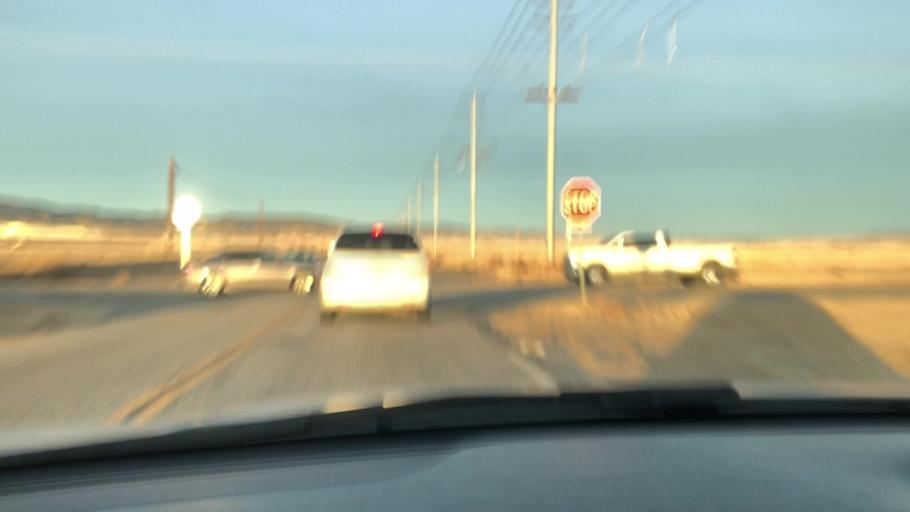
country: US
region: California
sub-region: Los Angeles County
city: Quartz Hill
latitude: 34.6748
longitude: -118.2537
